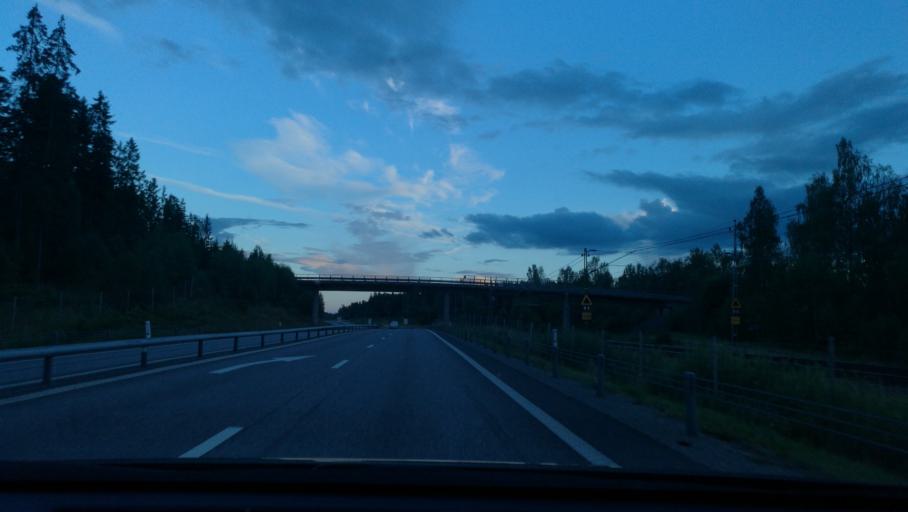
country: SE
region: Soedermanland
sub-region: Katrineholms Kommun
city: Katrineholm
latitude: 58.9260
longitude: 16.1959
